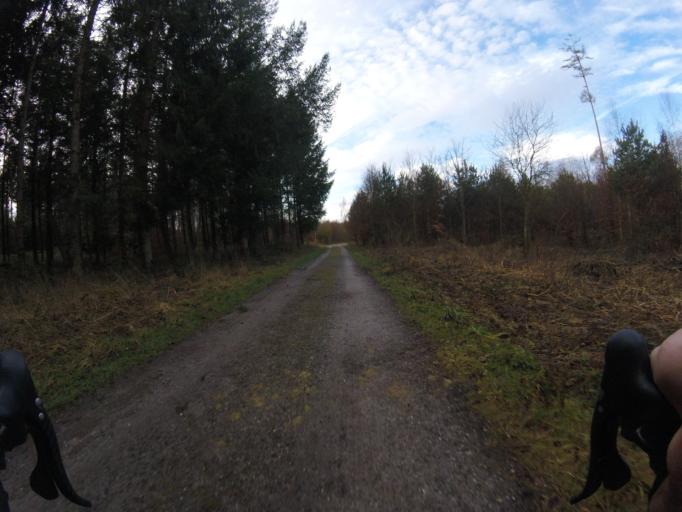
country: CH
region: Fribourg
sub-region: Sense District
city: Flamatt
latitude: 46.9110
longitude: 7.3416
